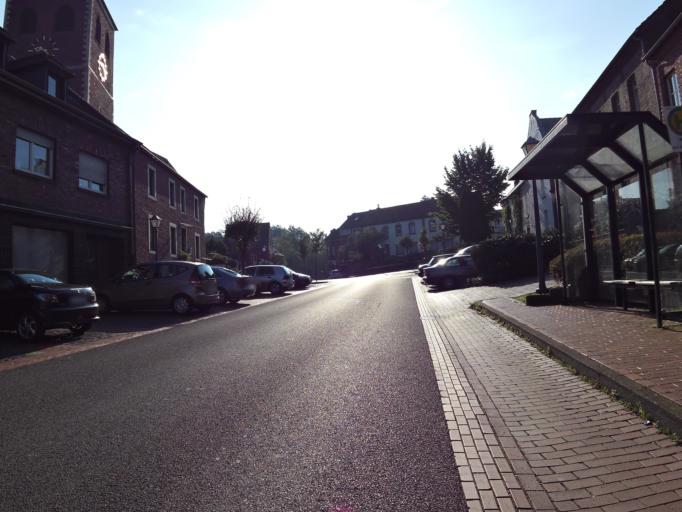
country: DE
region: North Rhine-Westphalia
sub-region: Regierungsbezirk Koln
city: Ubach-Palenberg
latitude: 50.9183
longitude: 6.1216
